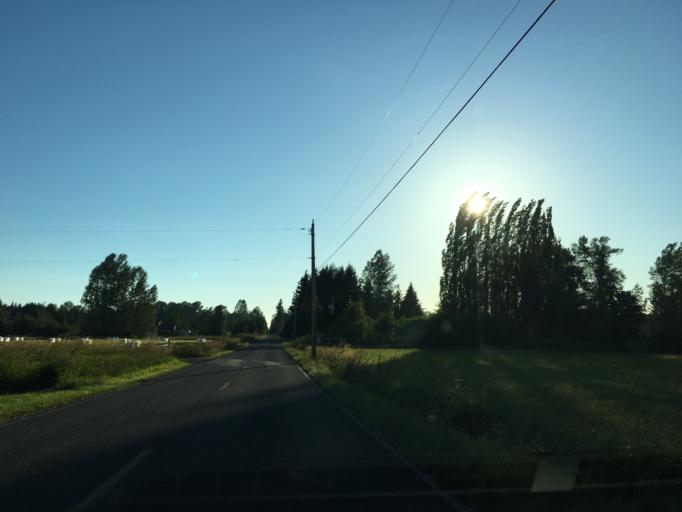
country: US
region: Washington
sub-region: Whatcom County
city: Geneva
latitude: 48.8181
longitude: -122.3447
